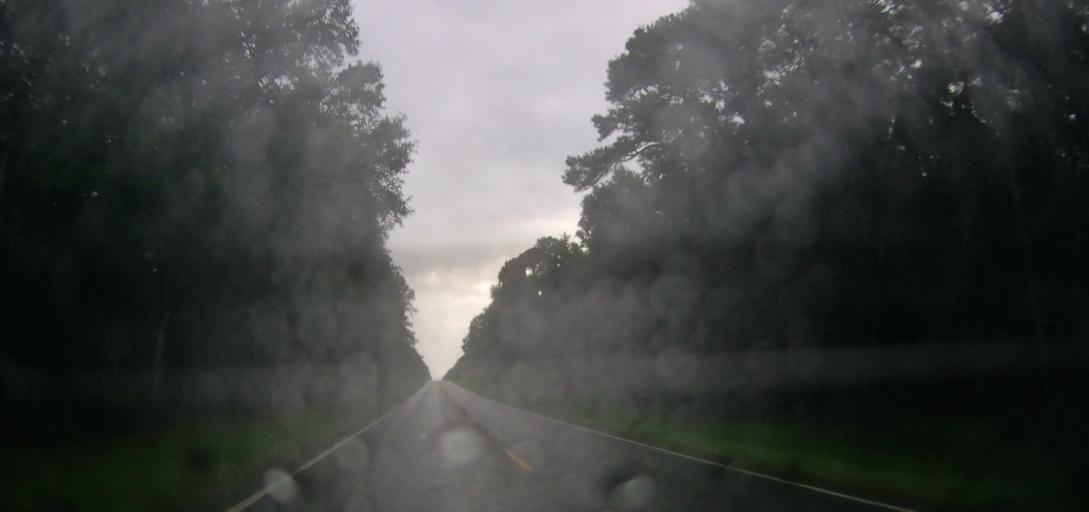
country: US
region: Georgia
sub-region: Brantley County
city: Nahunta
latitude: 31.3243
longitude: -81.7592
